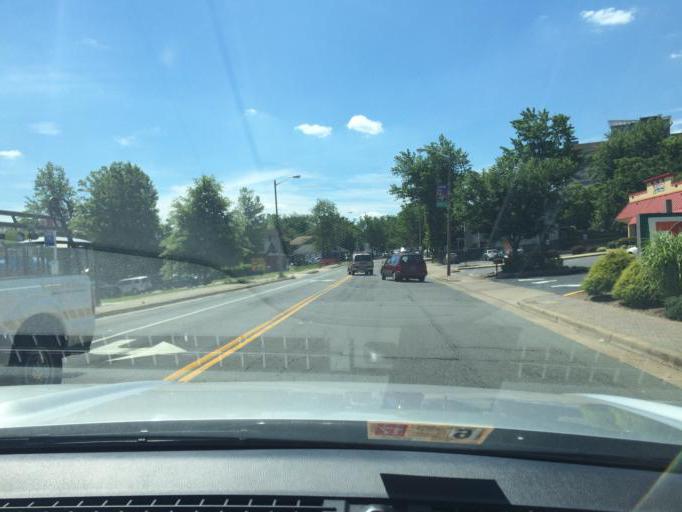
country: US
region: Virginia
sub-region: City of Alexandria
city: Alexandria
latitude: 38.8364
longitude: -77.0612
